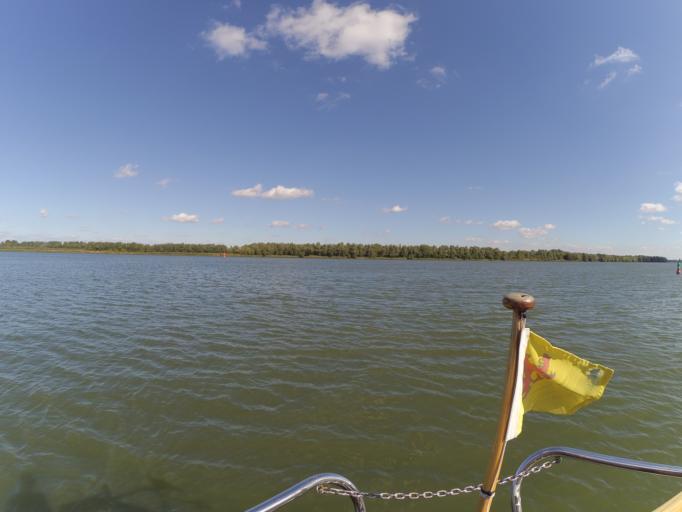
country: NL
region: South Holland
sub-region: Gemeente Oud-Beijerland
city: Oud-Beijerland
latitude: 51.8356
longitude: 4.4311
